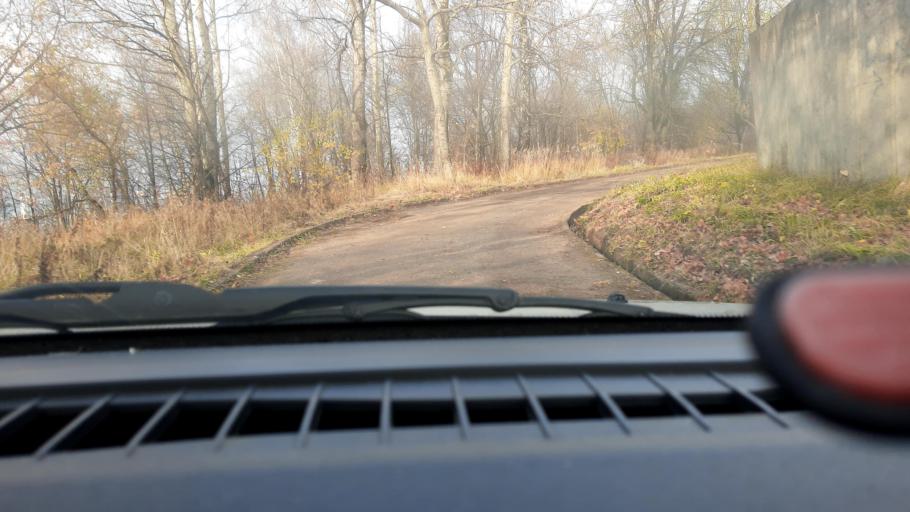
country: RU
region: Nizjnij Novgorod
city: Nizhniy Novgorod
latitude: 56.2898
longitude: 43.9723
